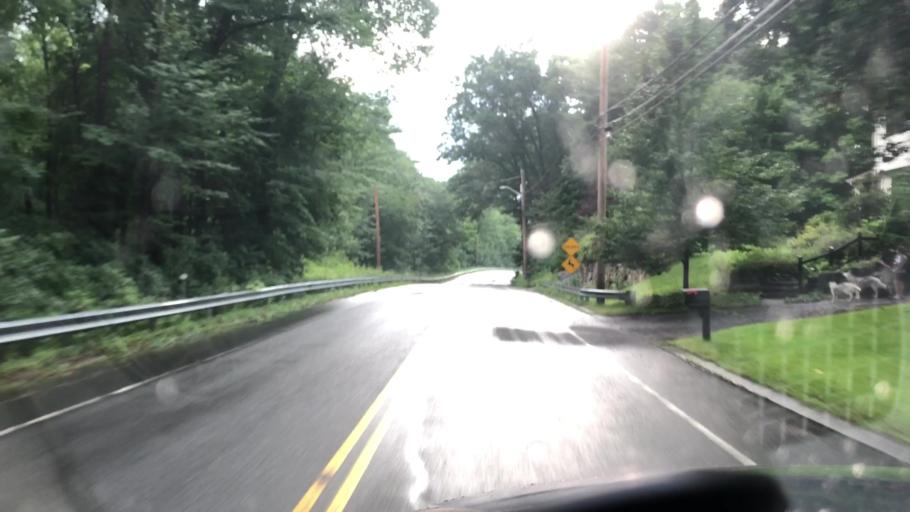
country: US
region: Massachusetts
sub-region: Hampshire County
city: Easthampton
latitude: 42.3009
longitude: -72.6759
